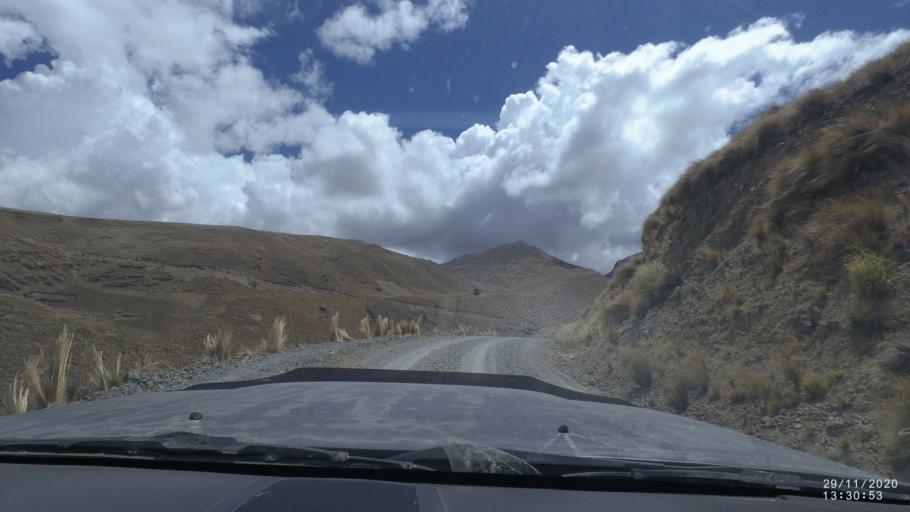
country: BO
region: Cochabamba
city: Cochabamba
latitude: -17.1031
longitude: -66.3415
